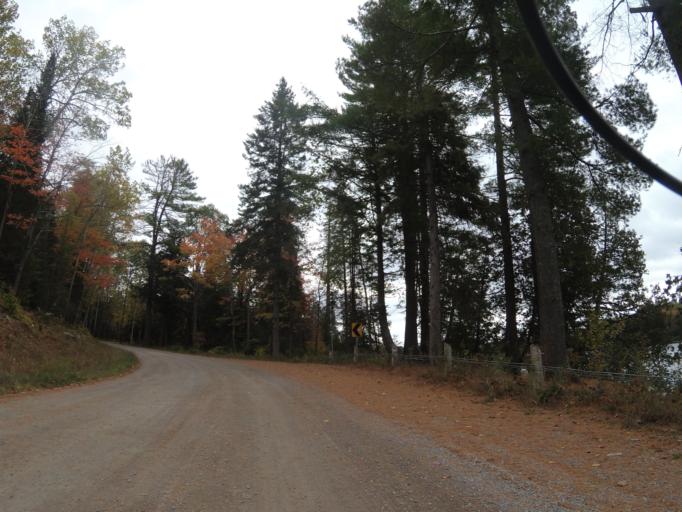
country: CA
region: Ontario
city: Renfrew
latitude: 45.2569
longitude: -77.1919
